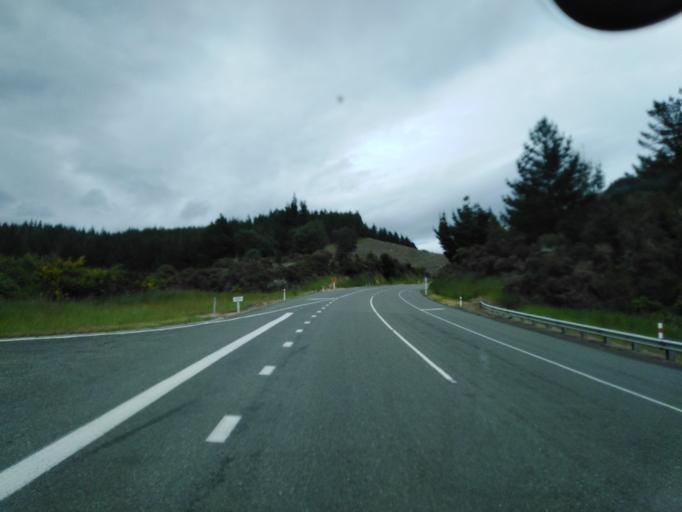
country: NZ
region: Tasman
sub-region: Tasman District
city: Wakefield
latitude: -41.4788
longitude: 172.9281
